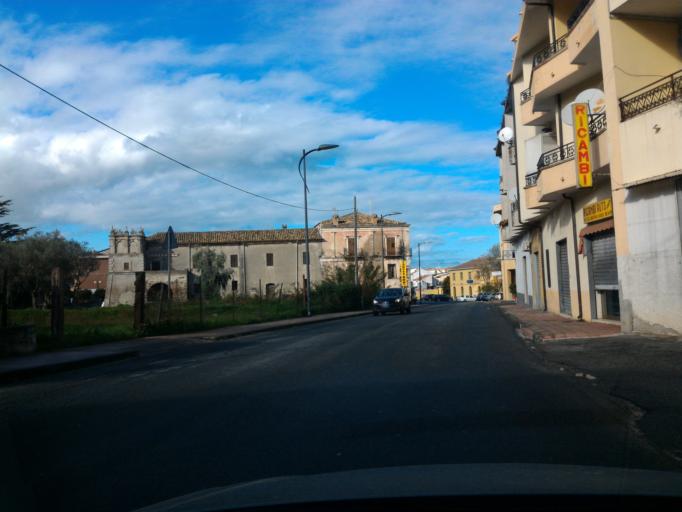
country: IT
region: Calabria
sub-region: Provincia di Crotone
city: Torretta
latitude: 39.4484
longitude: 17.0408
